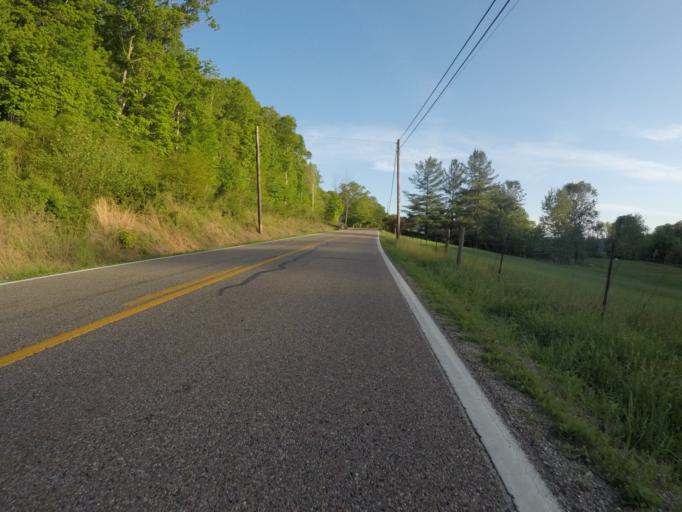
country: US
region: West Virginia
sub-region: Cabell County
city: Huntington
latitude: 38.5504
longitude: -82.4628
